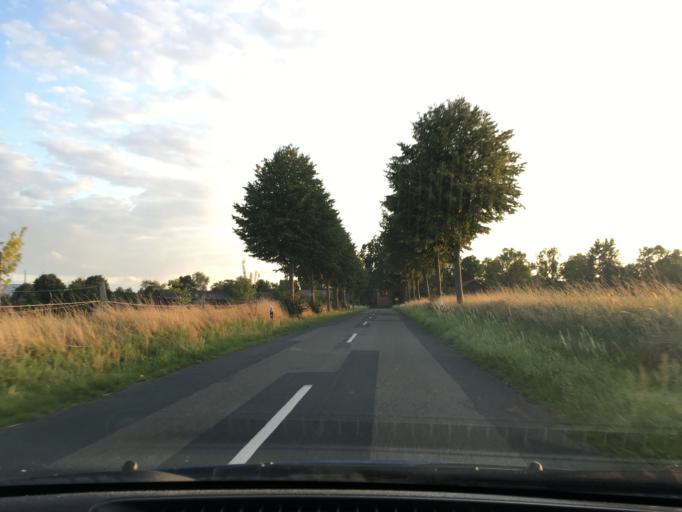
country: DE
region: Lower Saxony
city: Tosterglope
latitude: 53.2460
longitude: 10.7888
